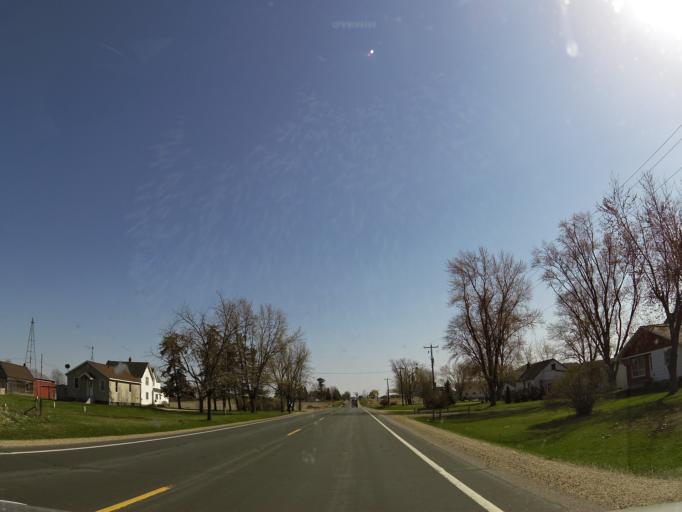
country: US
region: Wisconsin
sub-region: Pepin County
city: Durand
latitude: 44.7023
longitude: -91.9488
